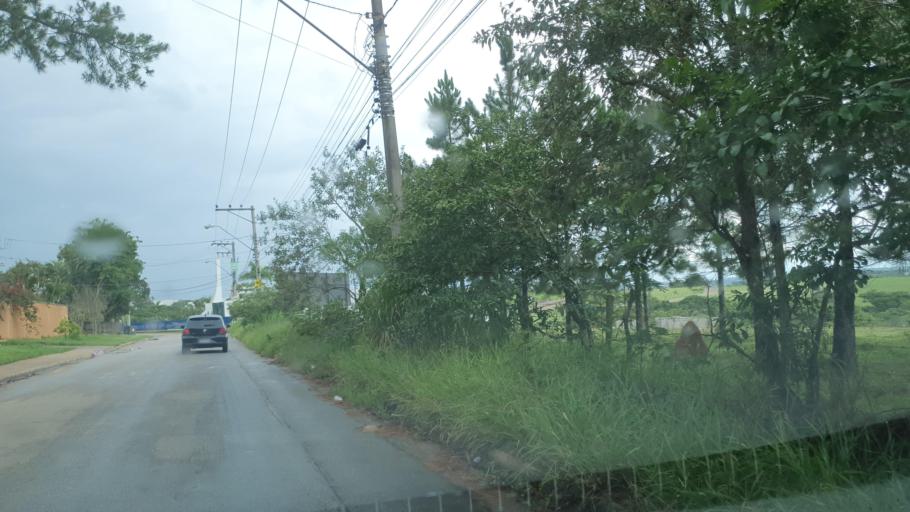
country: BR
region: Sao Paulo
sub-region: Sorocaba
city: Sorocaba
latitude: -23.5063
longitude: -47.5227
